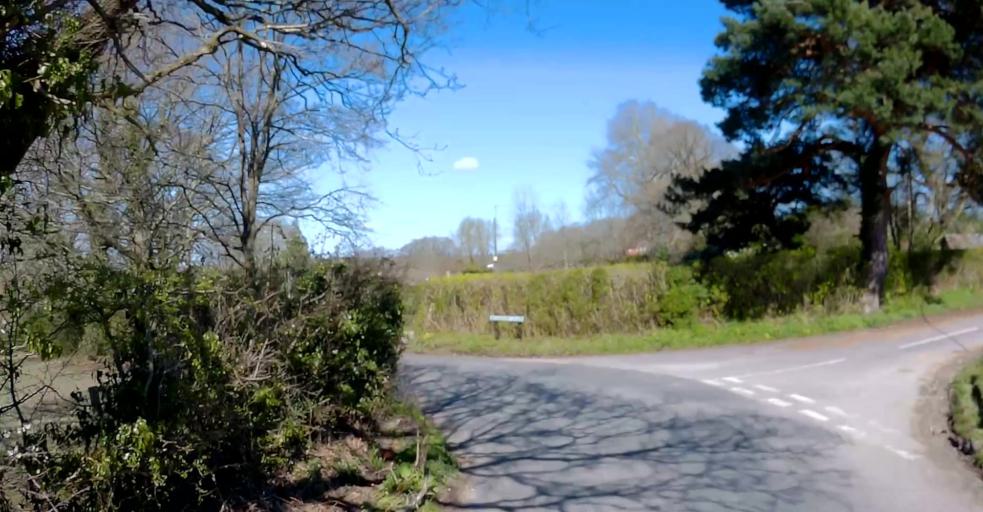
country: GB
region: England
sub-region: Hampshire
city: Lindford
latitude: 51.1631
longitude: -0.8288
